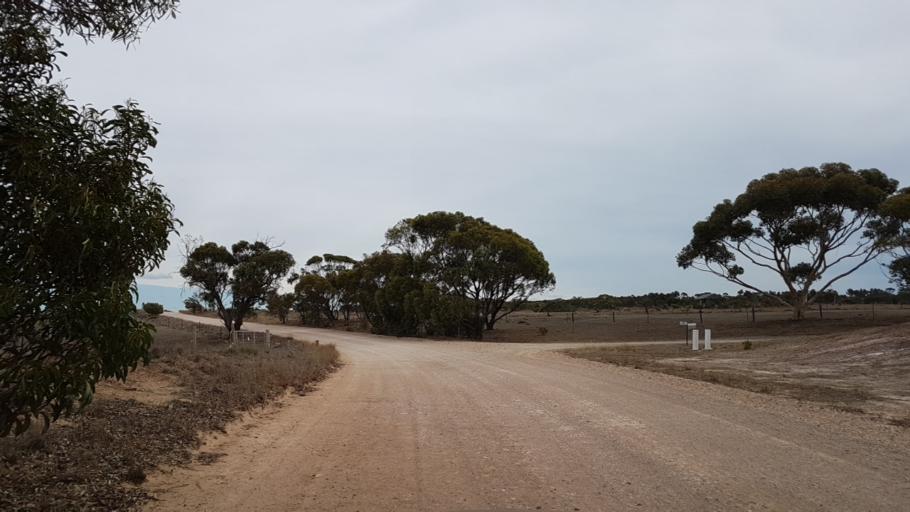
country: AU
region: South Australia
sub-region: Mount Barker
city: Callington
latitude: -35.0069
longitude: 139.0710
